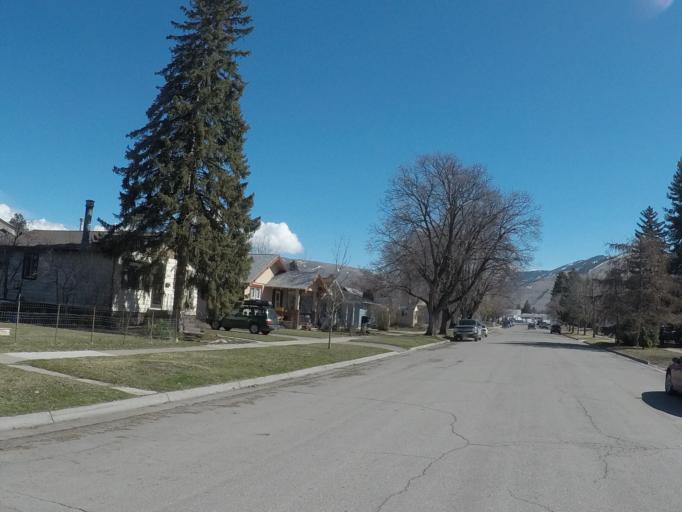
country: US
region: Montana
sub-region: Missoula County
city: Orchard Homes
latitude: 46.8595
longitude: -114.0222
